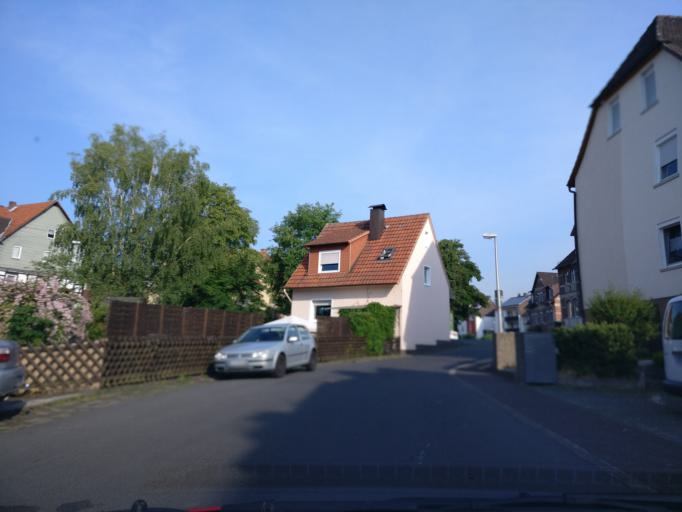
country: DE
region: Hesse
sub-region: Regierungsbezirk Kassel
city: Baunatal
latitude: 51.2749
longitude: 9.3740
